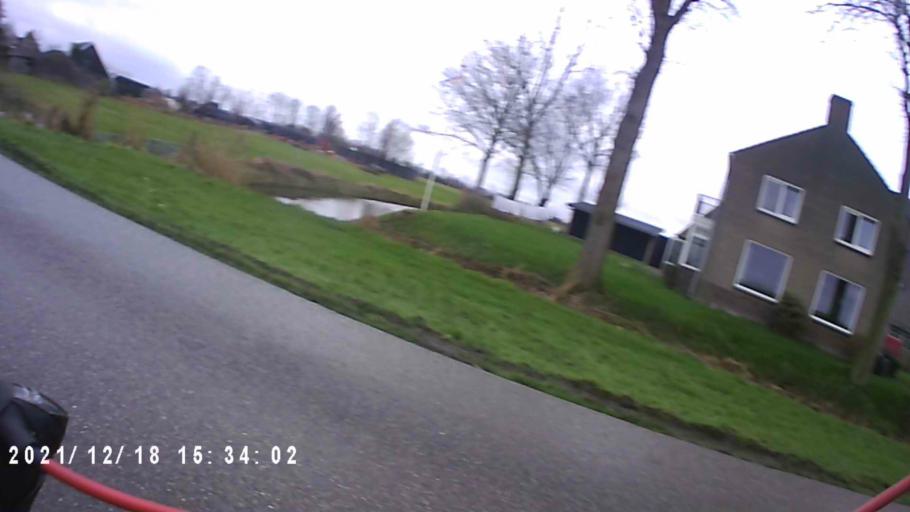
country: NL
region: Friesland
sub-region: Gemeente Dongeradeel
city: Anjum
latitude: 53.3452
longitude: 6.1366
